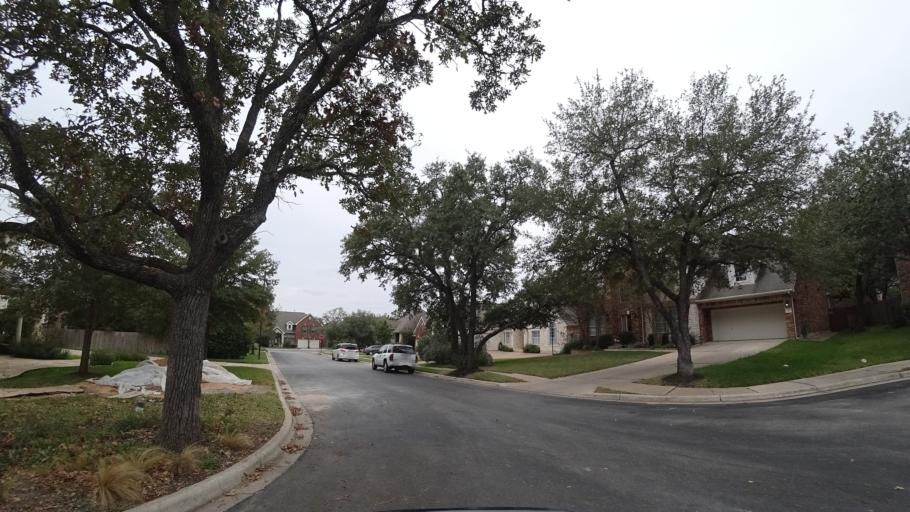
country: US
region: Texas
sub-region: Travis County
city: Shady Hollow
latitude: 30.1864
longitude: -97.9063
